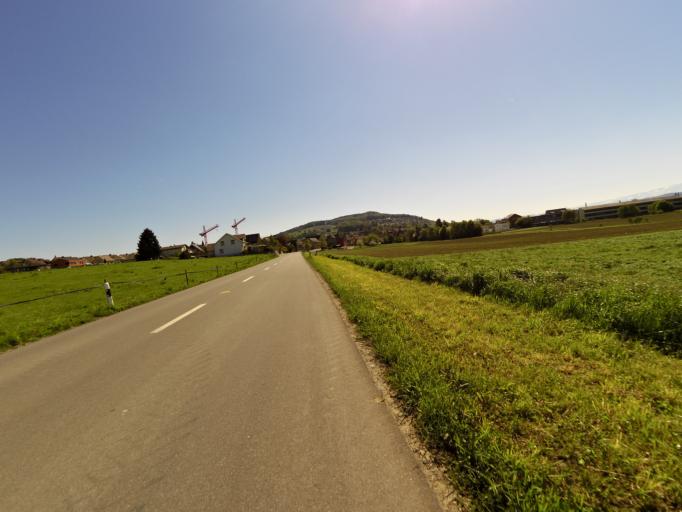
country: CH
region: Thurgau
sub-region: Weinfelden District
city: Maerstetten-Dorf
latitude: 47.5930
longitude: 9.0612
